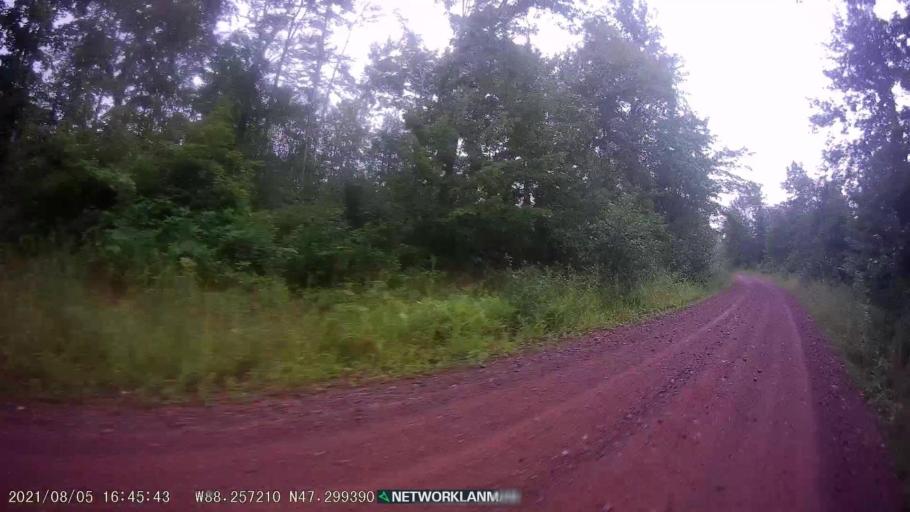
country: US
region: Michigan
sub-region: Keweenaw County
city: Eagle River
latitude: 47.2995
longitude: -88.2571
